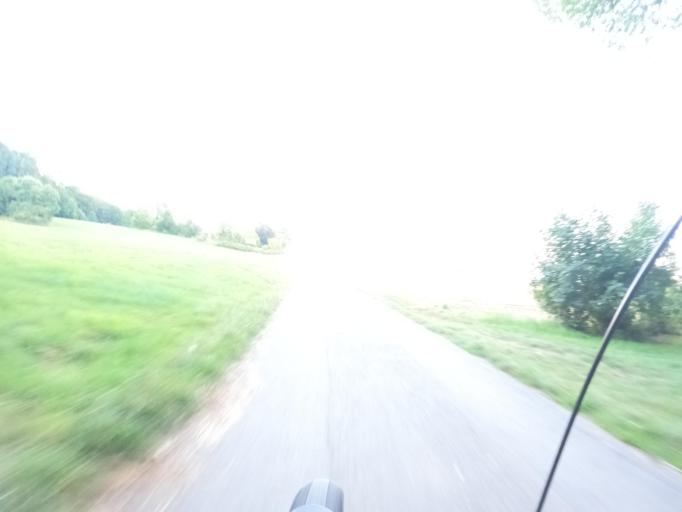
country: DE
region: Schleswig-Holstein
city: Steinberg
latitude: 54.7884
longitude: 9.7881
